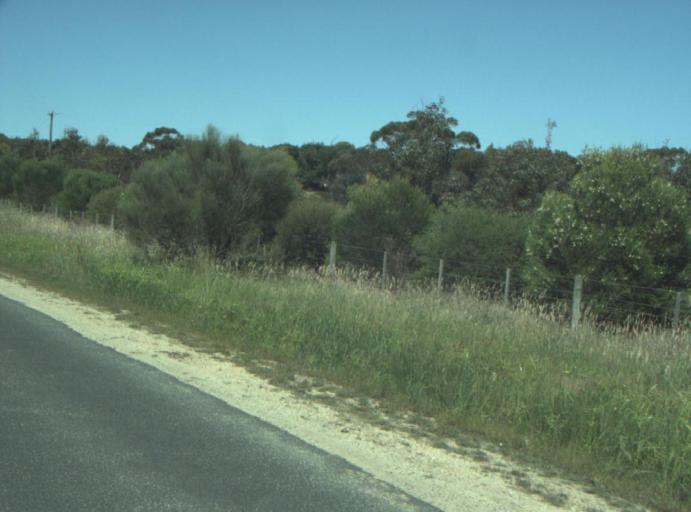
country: AU
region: Victoria
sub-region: Greater Geelong
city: Breakwater
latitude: -38.2493
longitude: 144.3511
